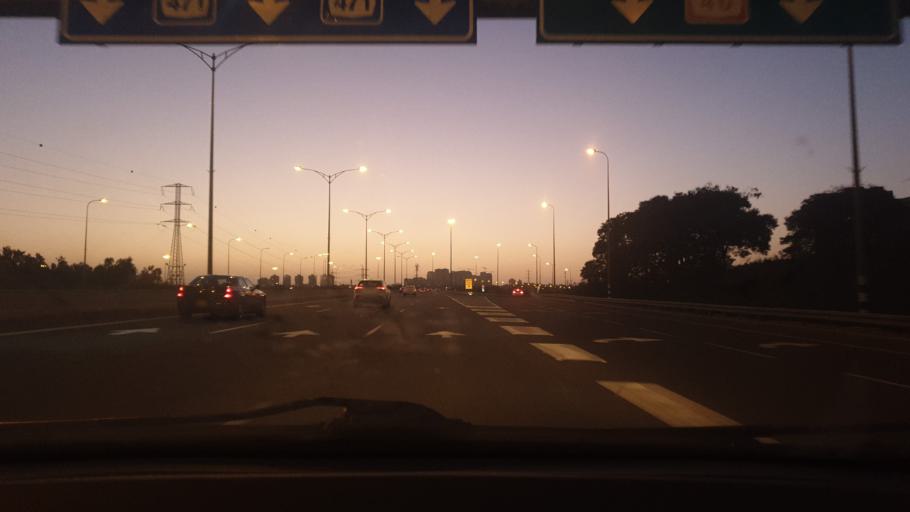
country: IL
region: Central District
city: Nehalim
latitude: 32.0671
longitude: 34.9092
